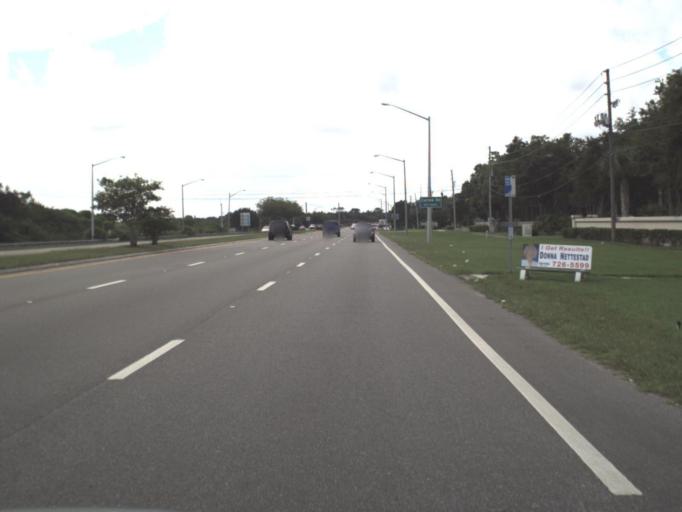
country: US
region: Florida
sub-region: Pinellas County
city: Saint George
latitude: 28.0538
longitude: -82.7110
